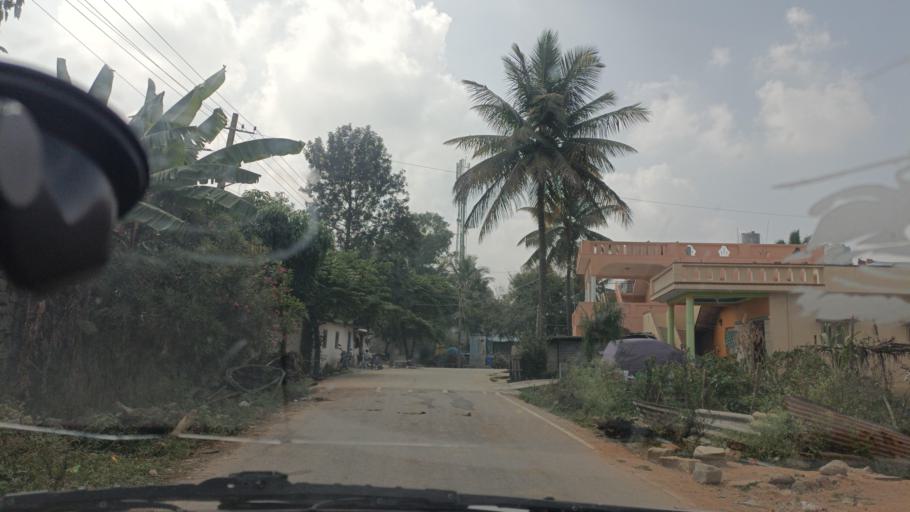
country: IN
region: Karnataka
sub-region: Bangalore Urban
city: Yelahanka
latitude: 13.1512
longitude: 77.6385
